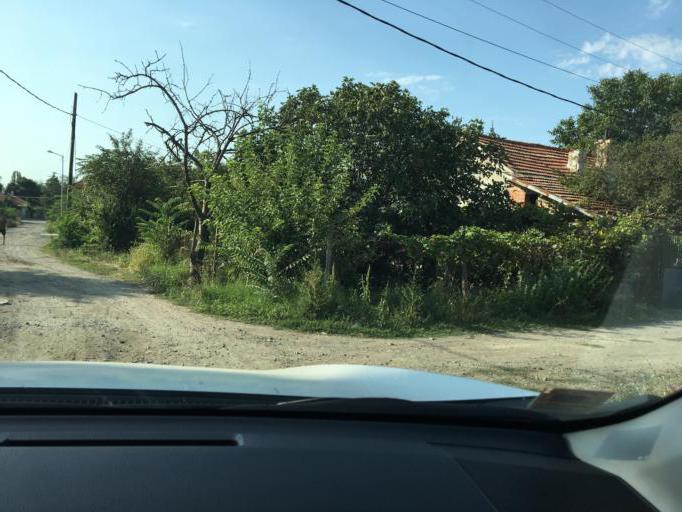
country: BG
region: Burgas
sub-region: Obshtina Burgas
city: Burgas
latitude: 42.6124
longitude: 27.4851
